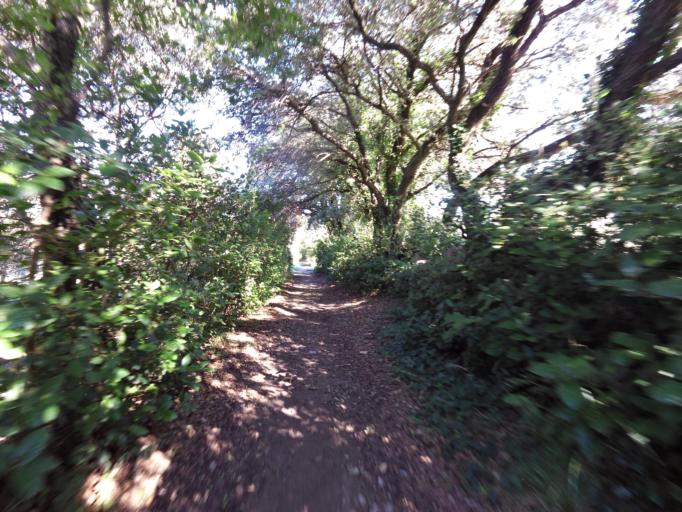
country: FR
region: Languedoc-Roussillon
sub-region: Departement du Gard
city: Aubais
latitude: 43.7449
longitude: 4.1463
